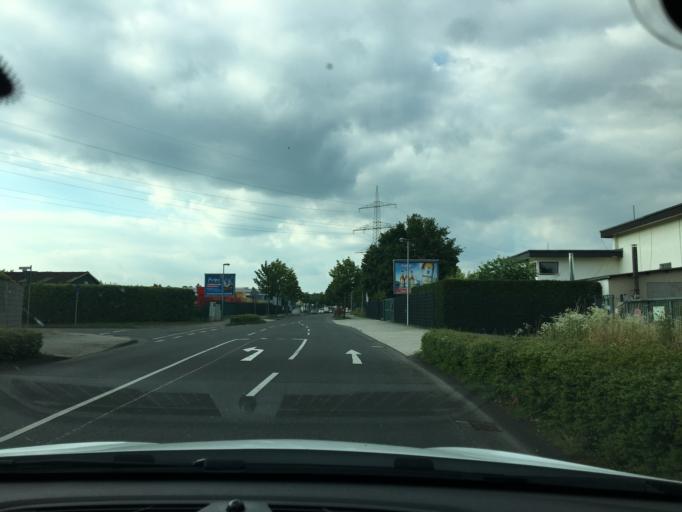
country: DE
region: North Rhine-Westphalia
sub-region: Regierungsbezirk Koln
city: Rosrath
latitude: 50.8853
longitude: 7.1843
